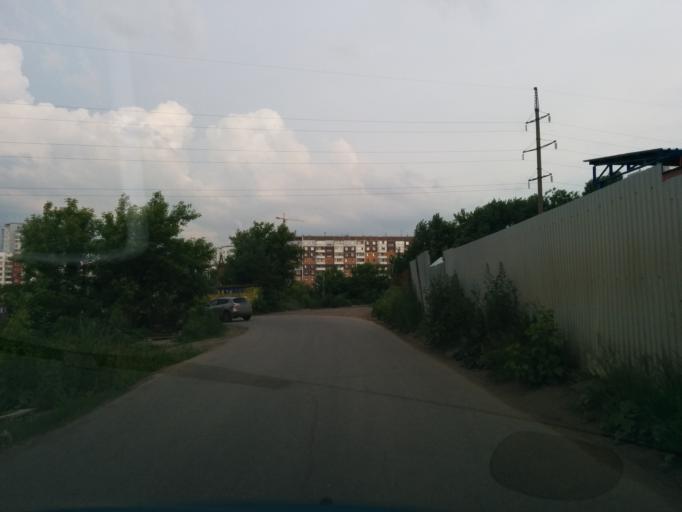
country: RU
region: Perm
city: Perm
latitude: 58.0140
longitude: 56.3043
